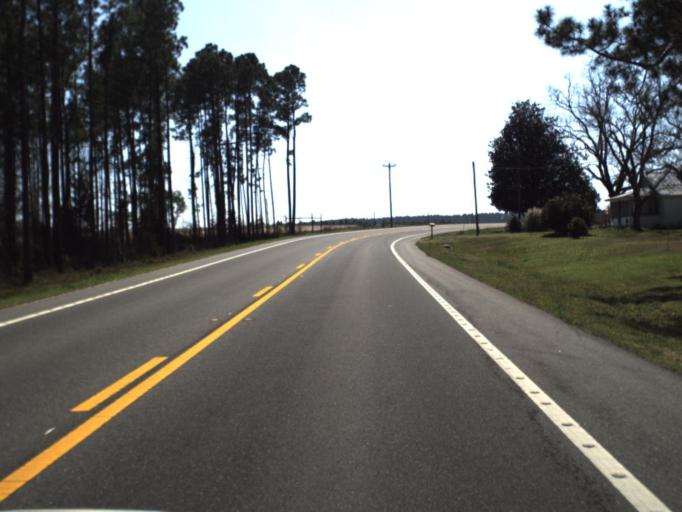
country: US
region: Florida
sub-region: Jackson County
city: Sneads
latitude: 30.6951
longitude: -85.0204
